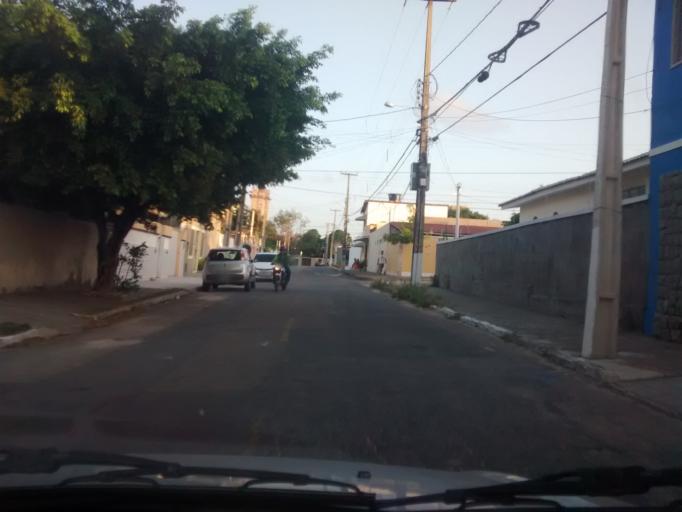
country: BR
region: Rio Grande do Norte
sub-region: Natal
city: Natal
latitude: -5.8730
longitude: -35.1860
